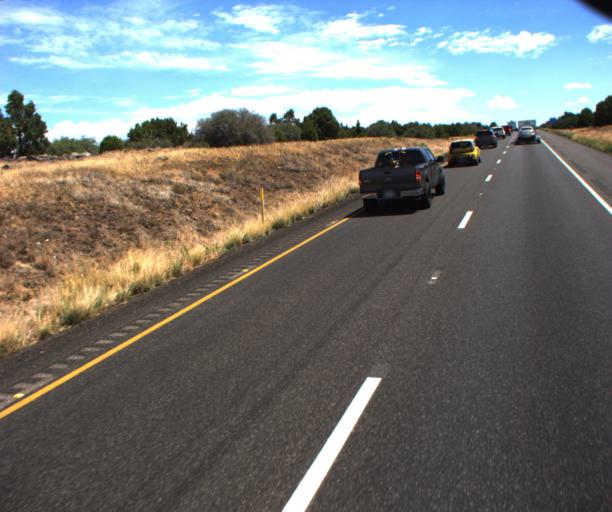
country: US
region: Arizona
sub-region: Yavapai County
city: Village of Oak Creek (Big Park)
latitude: 34.7423
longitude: -111.6878
